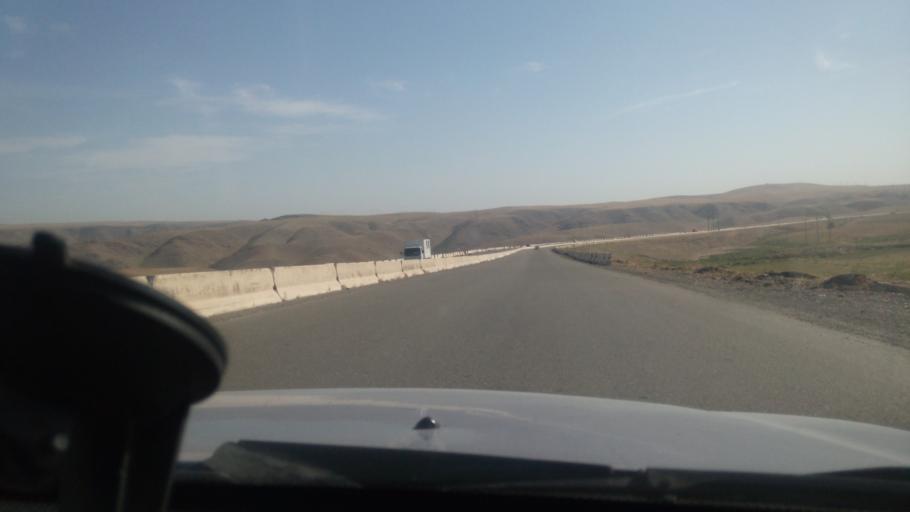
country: UZ
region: Jizzax
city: Jizzax
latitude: 40.0519
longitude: 67.6836
